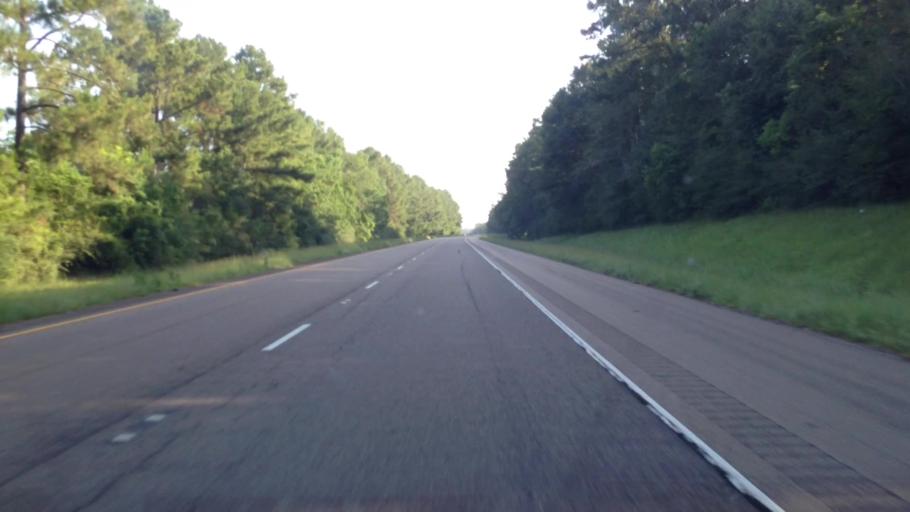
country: US
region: Louisiana
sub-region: Tangipahoa Parish
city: Roseland
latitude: 30.7947
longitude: -90.5329
